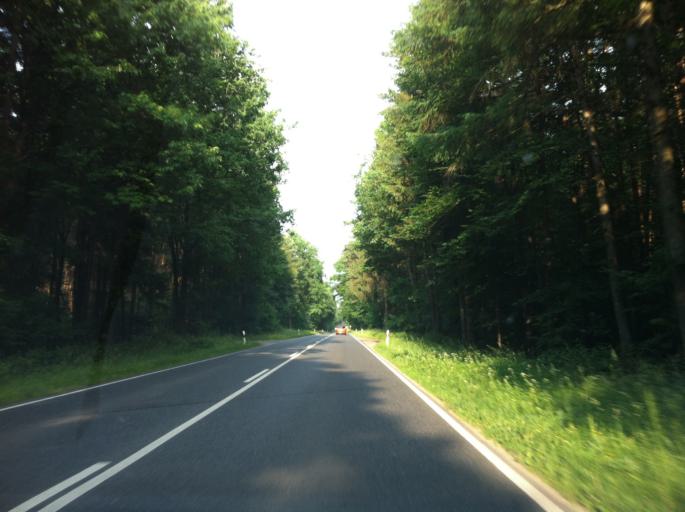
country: DE
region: Hesse
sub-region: Regierungsbezirk Darmstadt
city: Schaafheim
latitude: 49.9589
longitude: 9.0092
